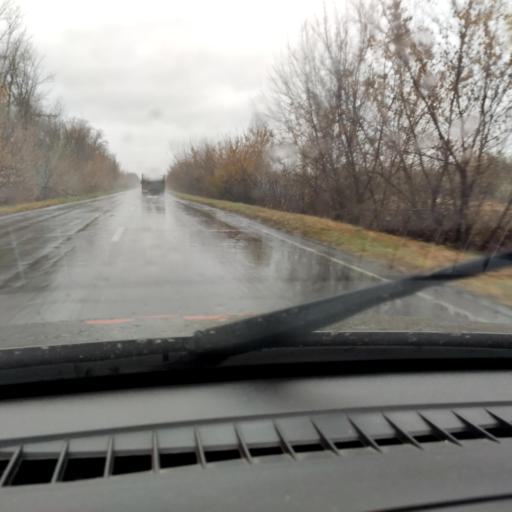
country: RU
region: Samara
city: Tol'yatti
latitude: 53.6926
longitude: 49.2481
